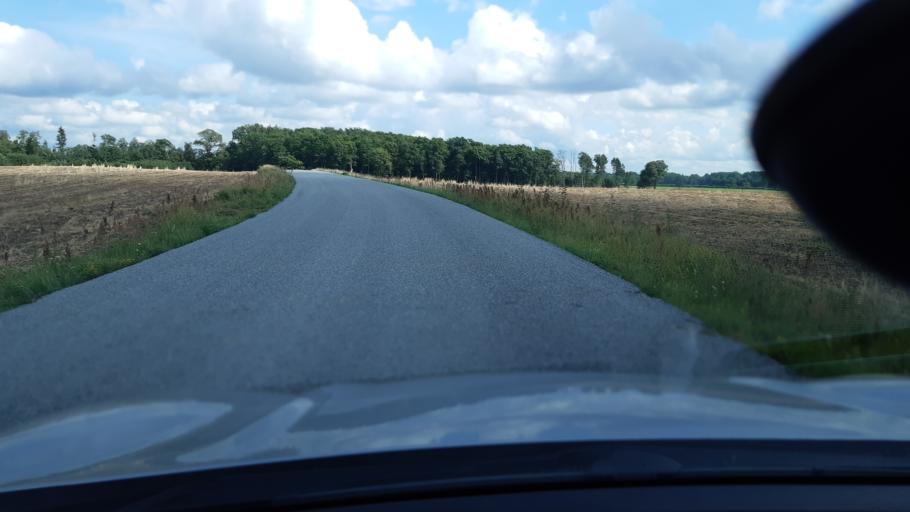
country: EE
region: Raplamaa
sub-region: Kehtna vald
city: Kehtna
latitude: 58.9037
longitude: 25.0889
